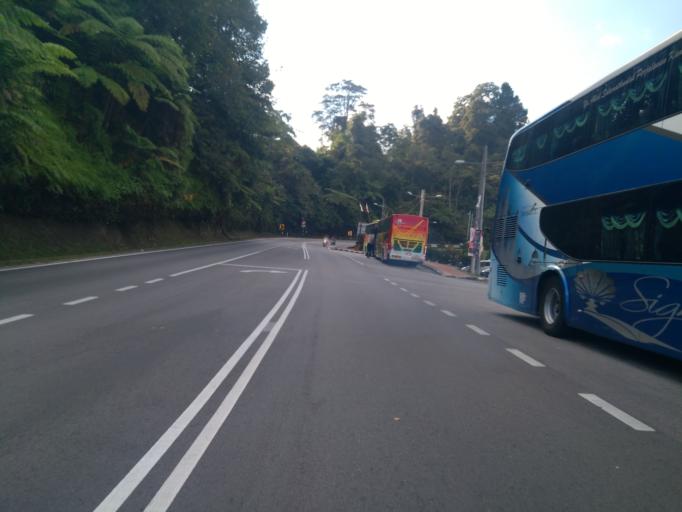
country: MY
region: Pahang
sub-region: Cameron Highlands
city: Tanah Rata
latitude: 4.4728
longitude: 101.3803
